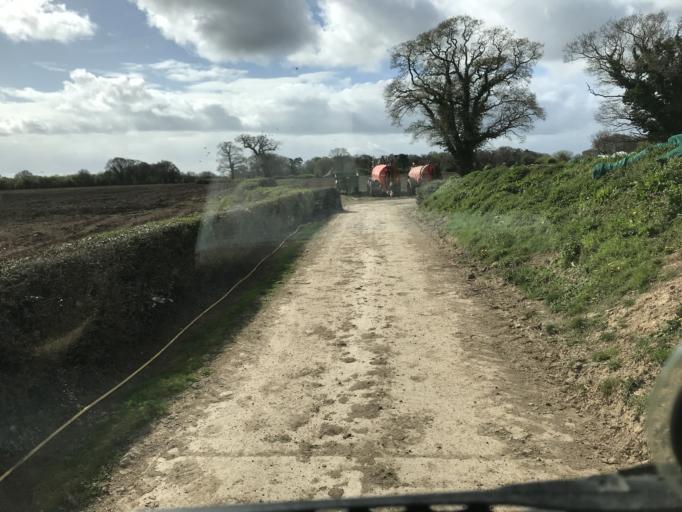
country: GB
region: England
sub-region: Cheshire West and Chester
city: Eccleston
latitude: 53.1515
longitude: -2.8883
